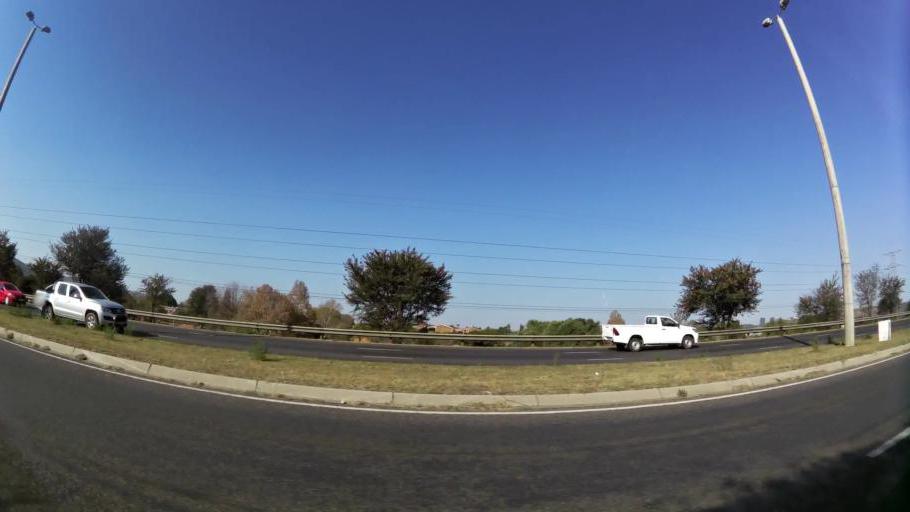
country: ZA
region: Gauteng
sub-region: City of Tshwane Metropolitan Municipality
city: Pretoria
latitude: -25.7111
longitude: 28.1719
